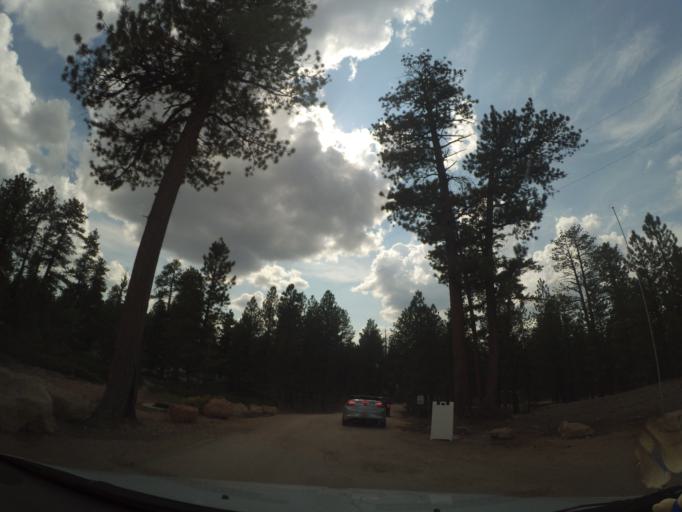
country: US
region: Utah
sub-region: Garfield County
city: Panguitch
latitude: 37.6228
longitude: -112.1729
